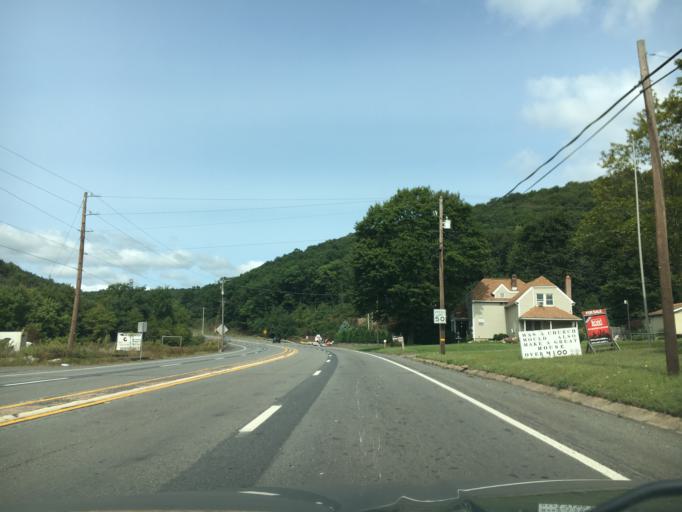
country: US
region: Pennsylvania
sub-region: Schuylkill County
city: Hometown
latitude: 40.8613
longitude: -76.0031
